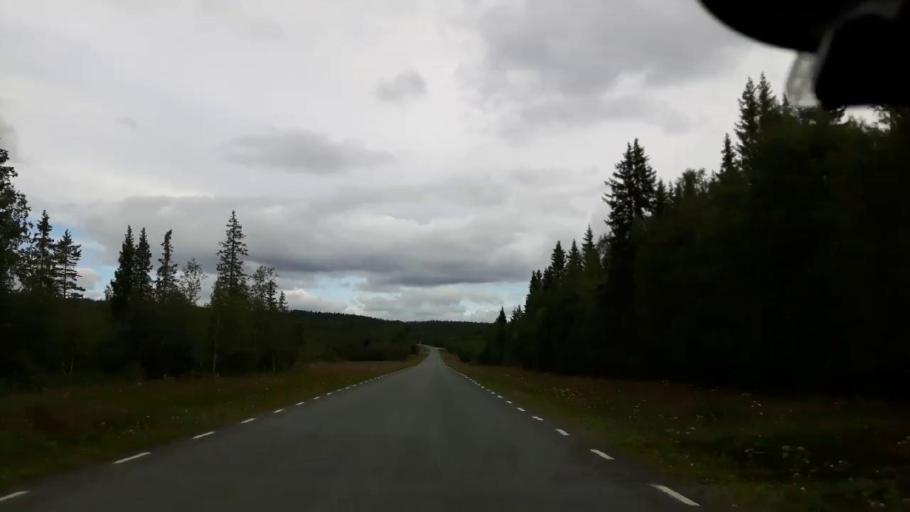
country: SE
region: Jaemtland
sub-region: Krokoms Kommun
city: Valla
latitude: 63.5642
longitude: 13.8449
